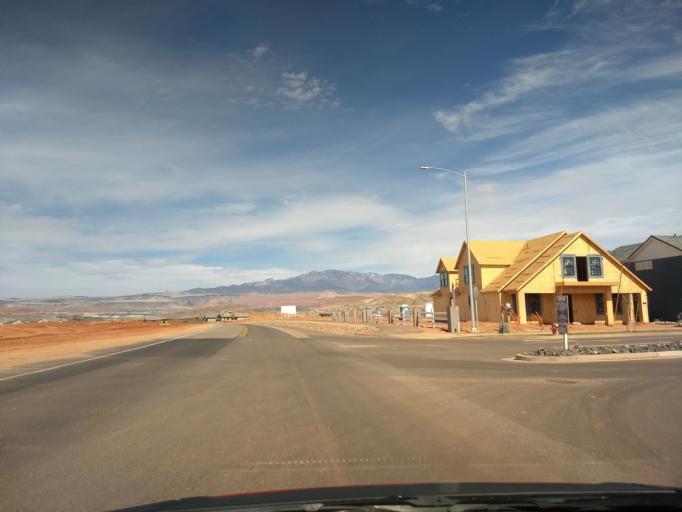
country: US
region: Utah
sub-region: Washington County
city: Washington
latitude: 37.0632
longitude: -113.4901
